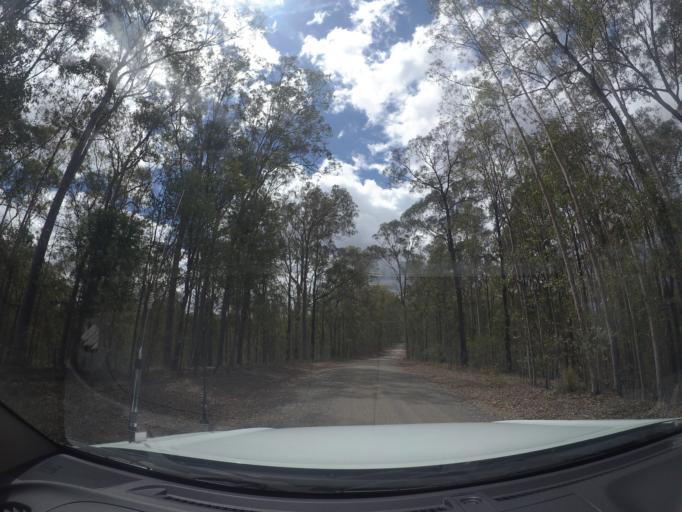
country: AU
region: Queensland
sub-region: Logan
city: Cedar Vale
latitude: -27.9068
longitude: 153.0307
